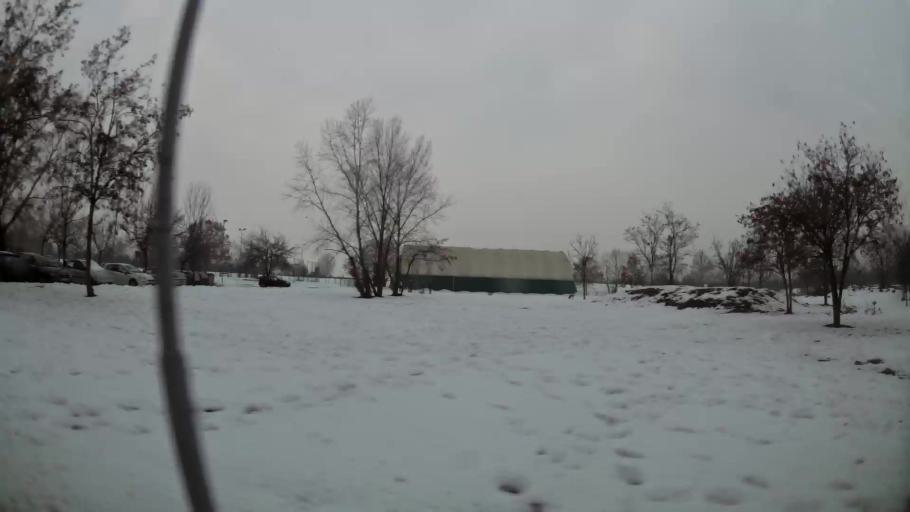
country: RS
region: Central Serbia
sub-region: Belgrade
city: Zemun
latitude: 44.8193
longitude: 20.3743
